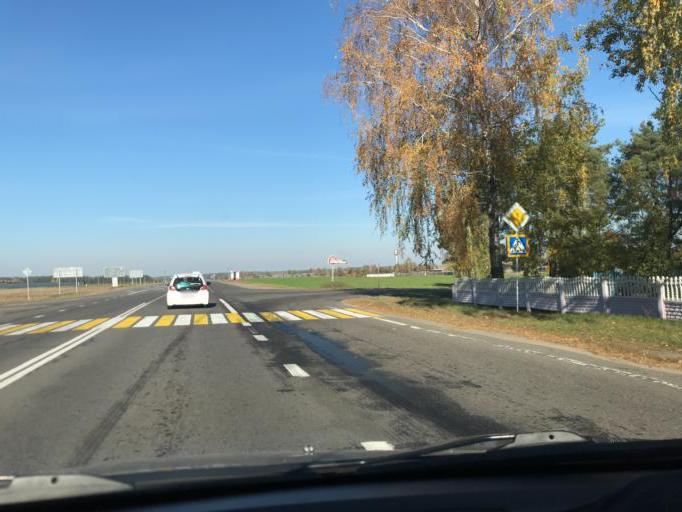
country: BY
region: Gomel
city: Parychy
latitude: 52.6279
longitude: 29.3771
